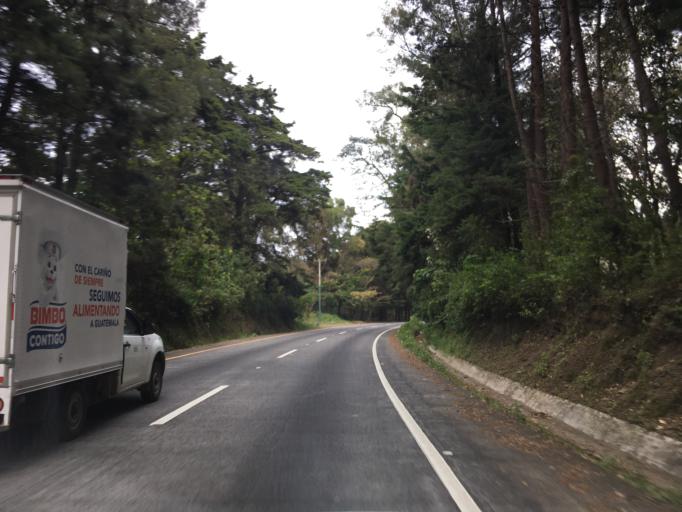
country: GT
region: Sacatepequez
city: Santa Lucia Milpas Altas
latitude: 14.5683
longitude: -90.6760
